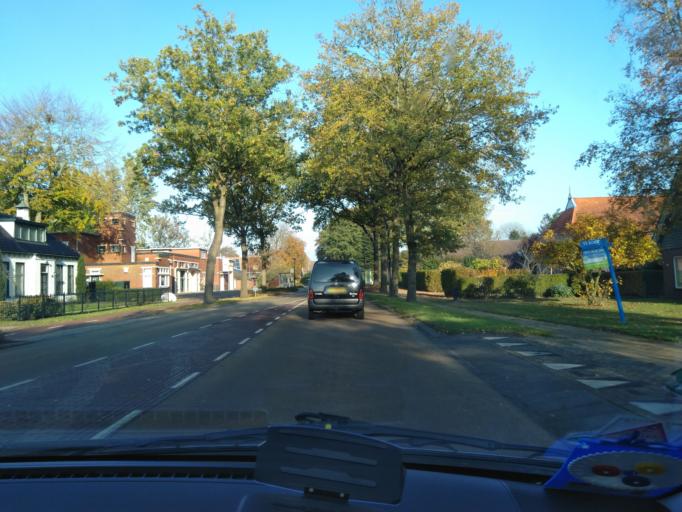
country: NL
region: Drenthe
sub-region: Gemeente Tynaarlo
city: Zuidlaren
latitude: 53.1088
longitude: 6.7083
